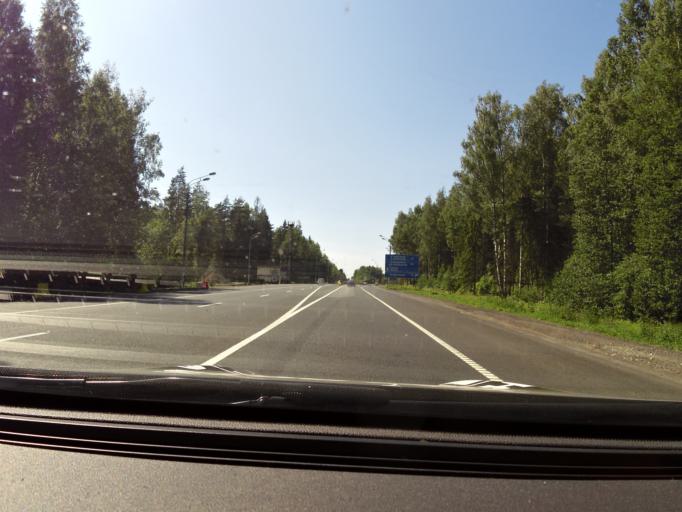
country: RU
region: Novgorod
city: Proletariy
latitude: 58.3948
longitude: 31.8906
